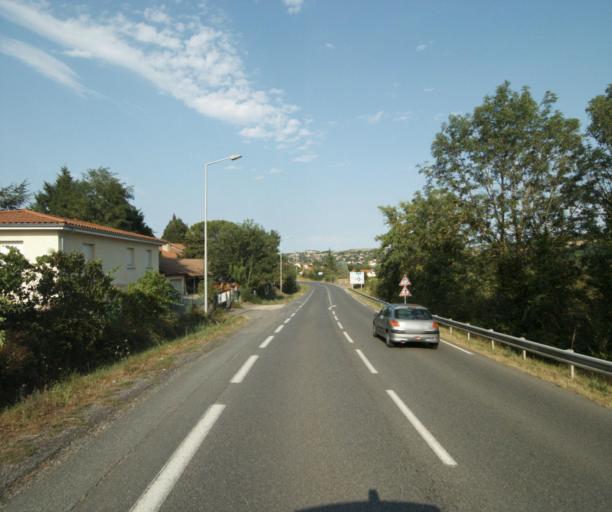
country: FR
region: Rhone-Alpes
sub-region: Departement du Rhone
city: Sain-Bel
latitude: 45.8279
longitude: 4.6020
